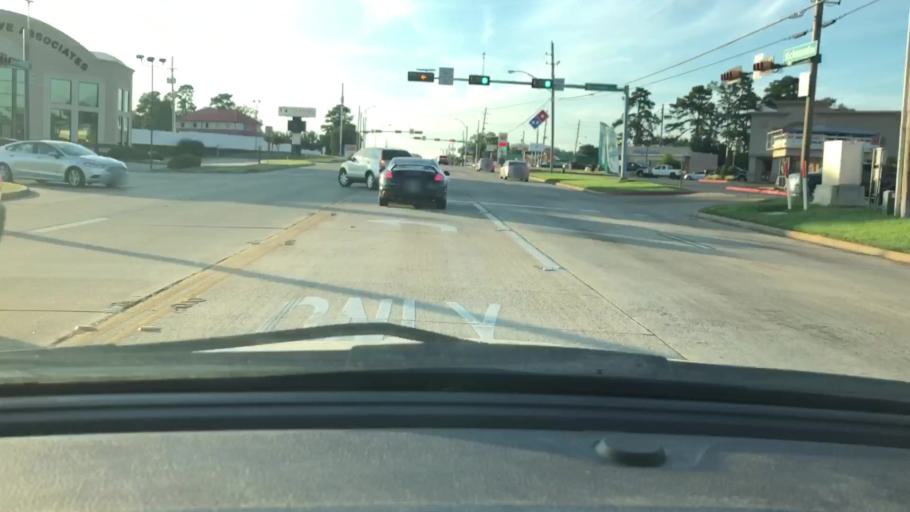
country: US
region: Texas
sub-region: Bowie County
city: Wake Village
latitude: 33.4592
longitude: -94.0895
